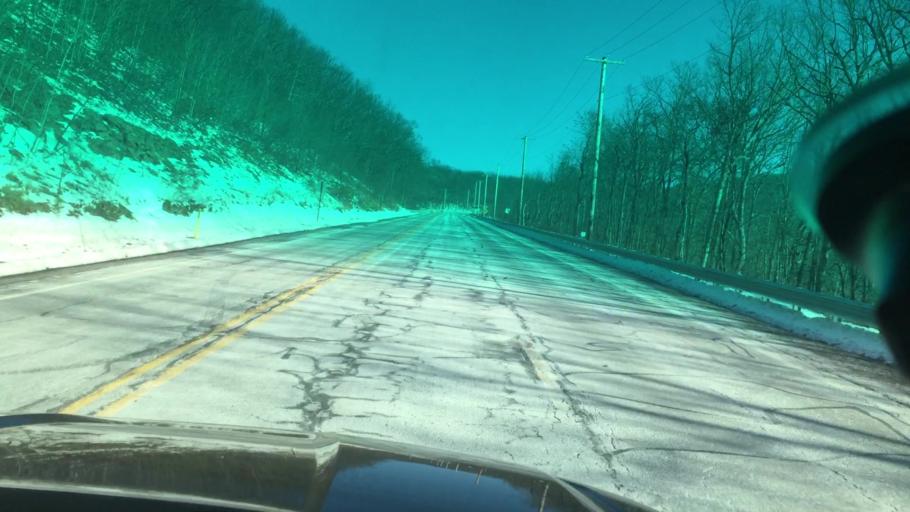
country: US
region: Pennsylvania
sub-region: Luzerne County
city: Oakdale
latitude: 41.0188
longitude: -75.9383
